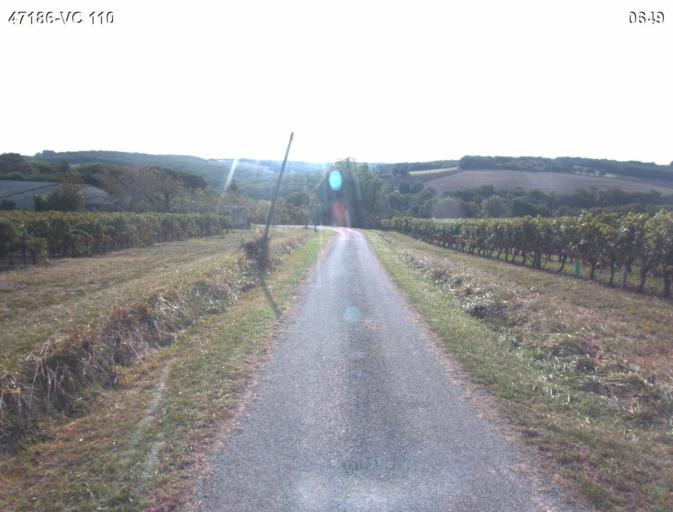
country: FR
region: Aquitaine
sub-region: Departement du Lot-et-Garonne
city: Port-Sainte-Marie
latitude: 44.1889
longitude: 0.4371
